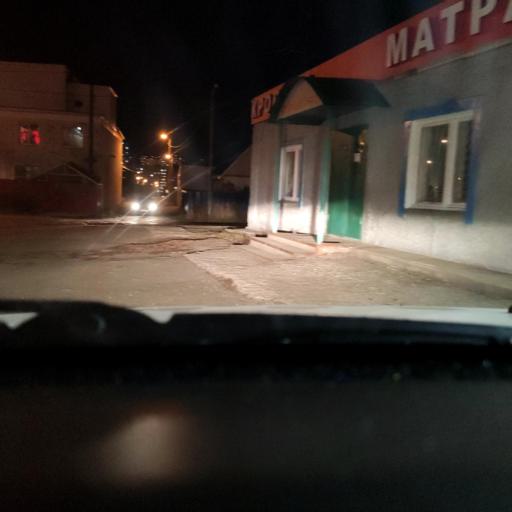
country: RU
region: Perm
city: Kondratovo
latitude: 57.9619
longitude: 56.1623
